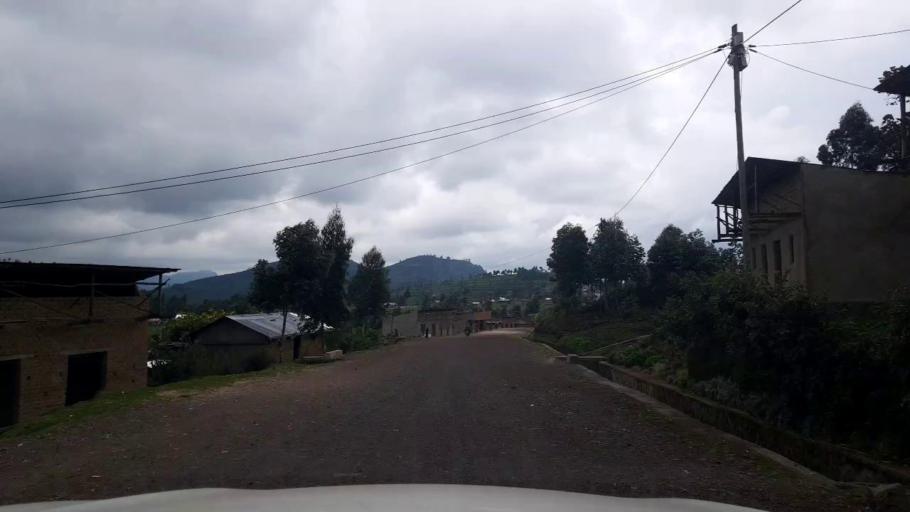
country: RW
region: Northern Province
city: Musanze
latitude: -1.5765
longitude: 29.4886
